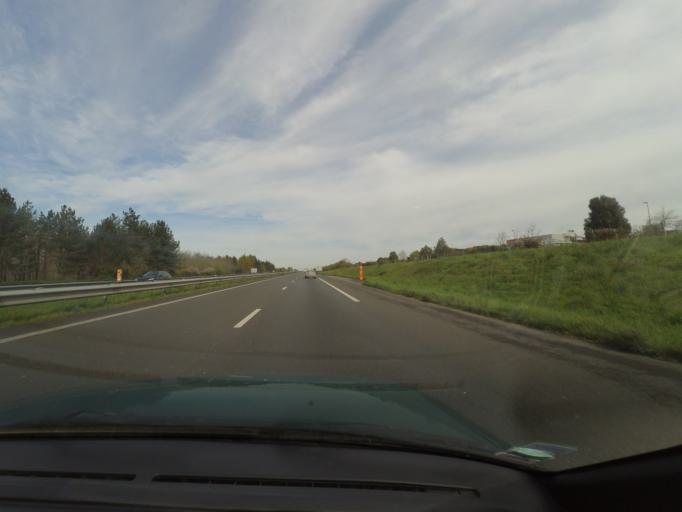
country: FR
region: Pays de la Loire
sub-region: Departement de la Loire-Atlantique
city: Le Bignon
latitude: 47.1204
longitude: -1.4969
